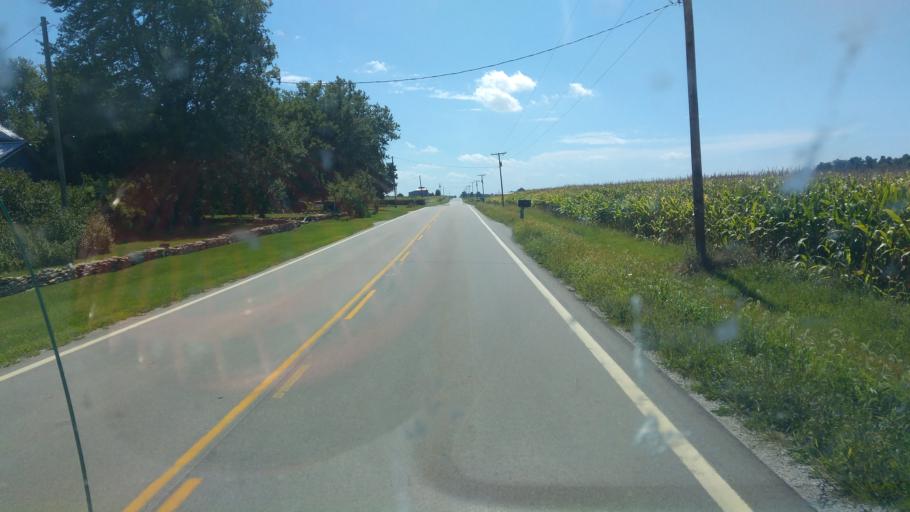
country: US
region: Ohio
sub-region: Wyandot County
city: Upper Sandusky
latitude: 40.8028
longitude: -83.1308
